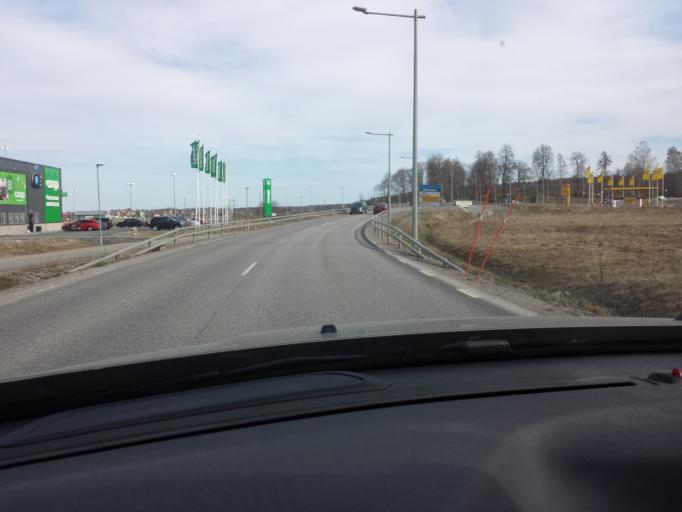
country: SE
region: OErebro
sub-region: Orebro Kommun
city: Orebro
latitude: 59.2509
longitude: 15.1942
